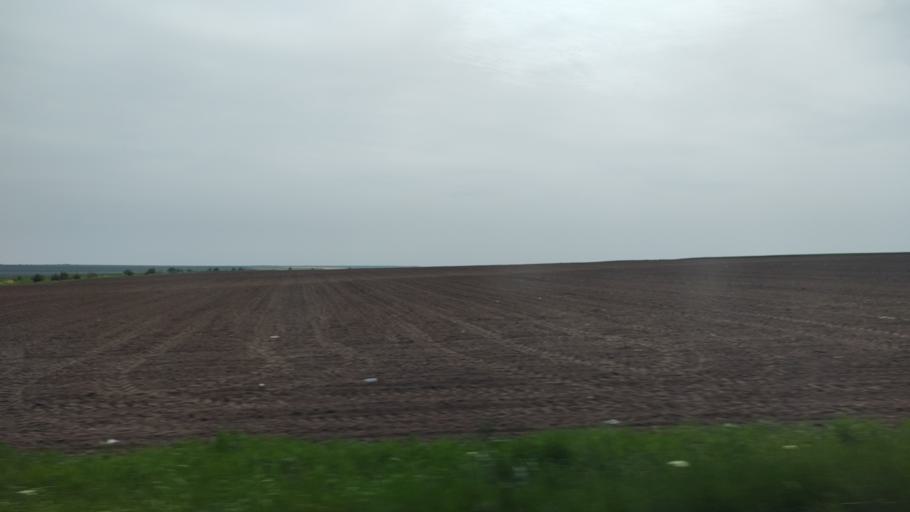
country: RO
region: Constanta
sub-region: Comuna Ciocarlia
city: Ciocarlia de Sus
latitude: 44.1329
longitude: 28.3461
